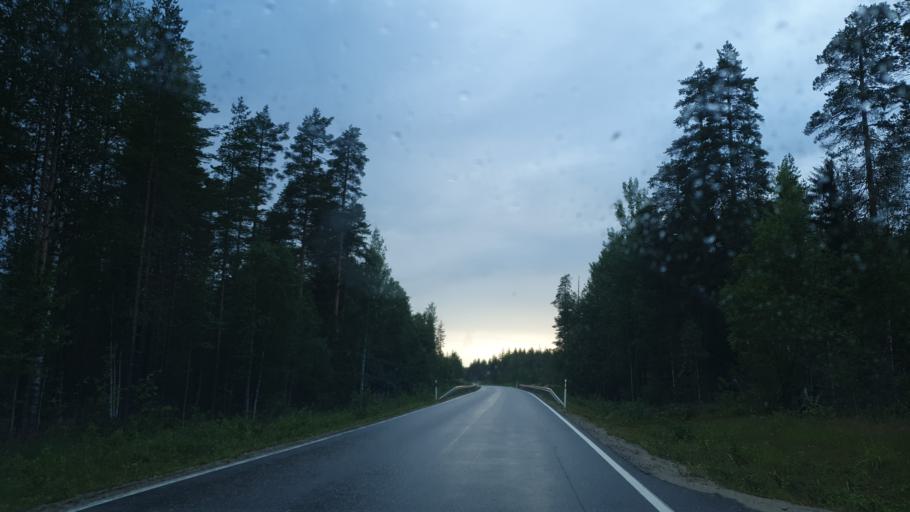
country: FI
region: North Karelia
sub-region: Pielisen Karjala
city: Lieksa
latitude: 63.5834
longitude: 29.9079
